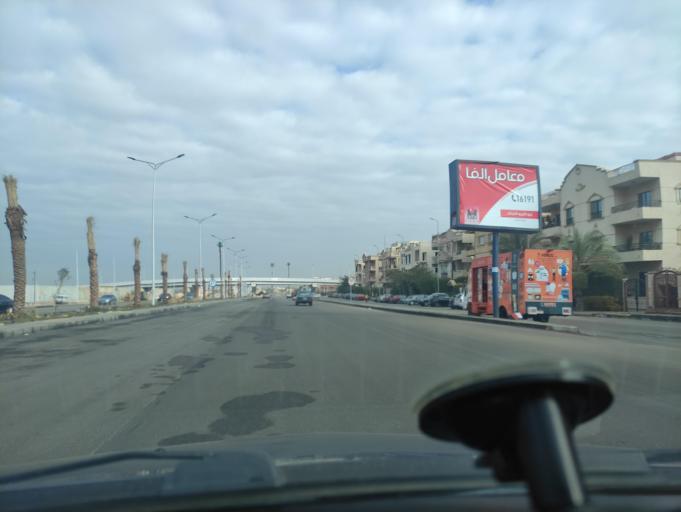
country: EG
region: Muhafazat al Qalyubiyah
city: Al Khankah
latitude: 30.0490
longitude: 31.4426
